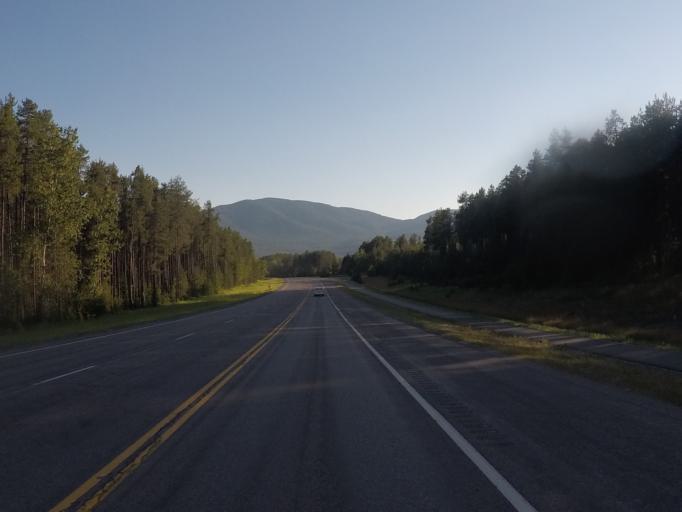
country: US
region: Montana
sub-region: Flathead County
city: Columbia Falls
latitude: 48.4488
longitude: -114.0300
